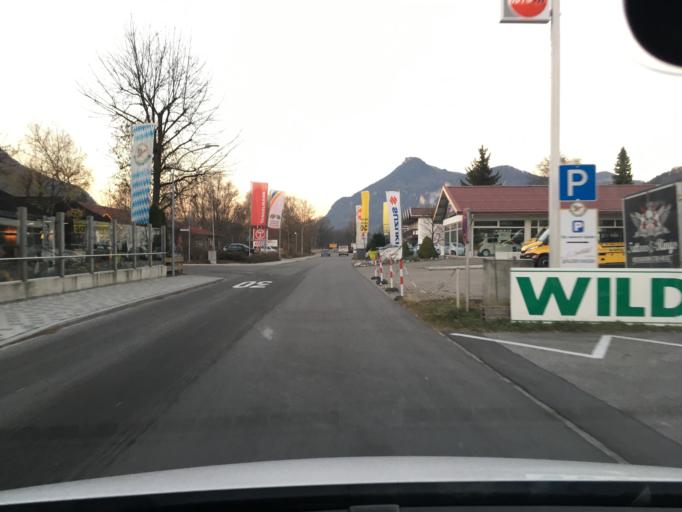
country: DE
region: Bavaria
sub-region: Upper Bavaria
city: Oberaudorf
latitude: 47.6477
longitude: 12.1791
